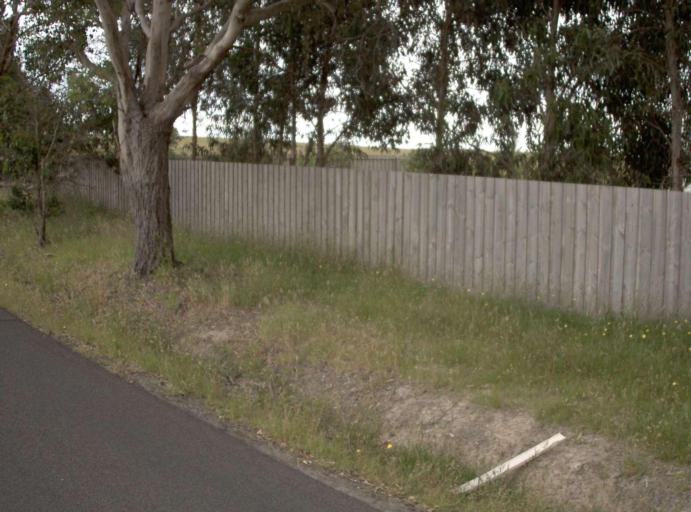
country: AU
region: Victoria
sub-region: Bass Coast
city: Cowes
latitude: -38.4219
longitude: 145.4375
